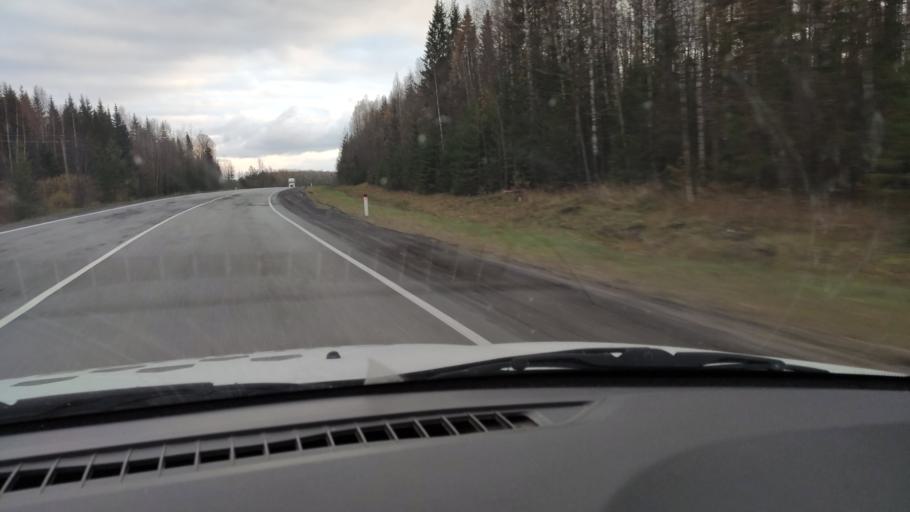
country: RU
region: Kirov
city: Omutninsk
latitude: 58.7540
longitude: 52.0458
